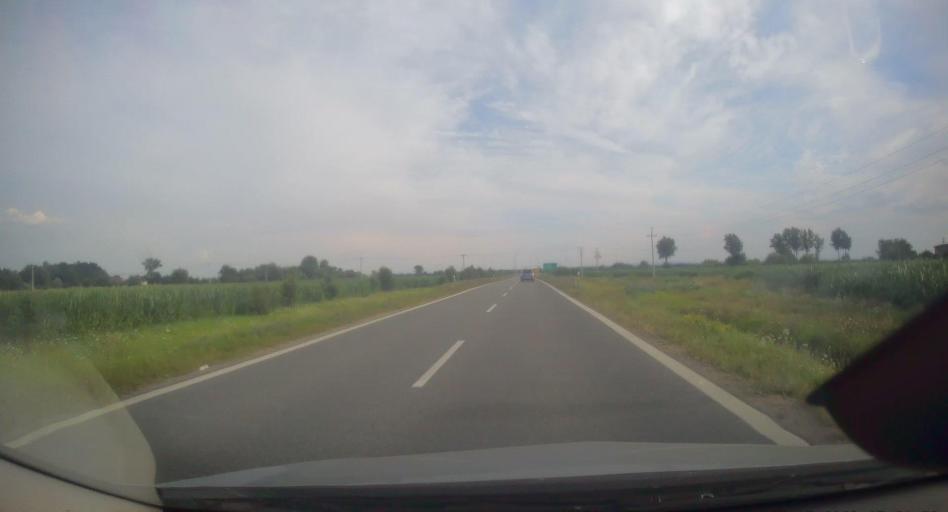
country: PL
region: Lesser Poland Voivodeship
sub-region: Powiat brzeski
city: Szczurowa
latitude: 50.1265
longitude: 20.6125
